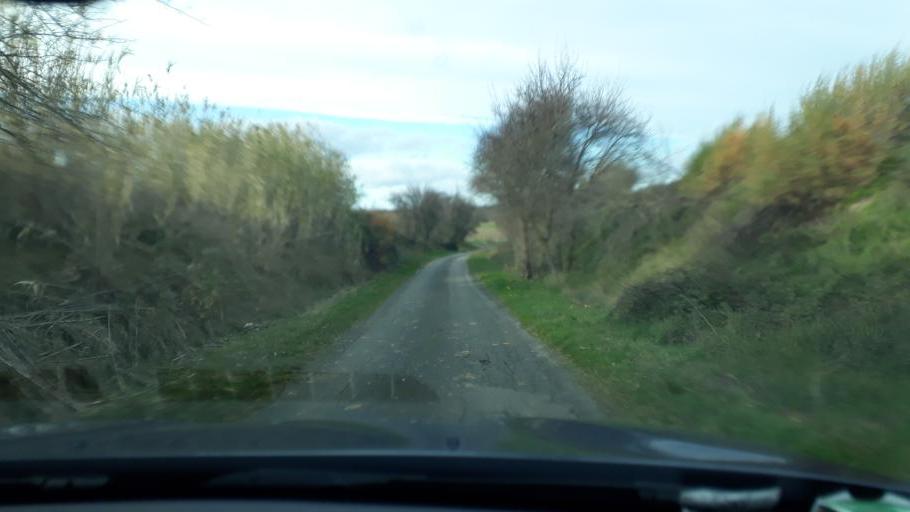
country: FR
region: Languedoc-Roussillon
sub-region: Departement de l'Herault
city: Florensac
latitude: 43.4000
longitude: 3.4594
